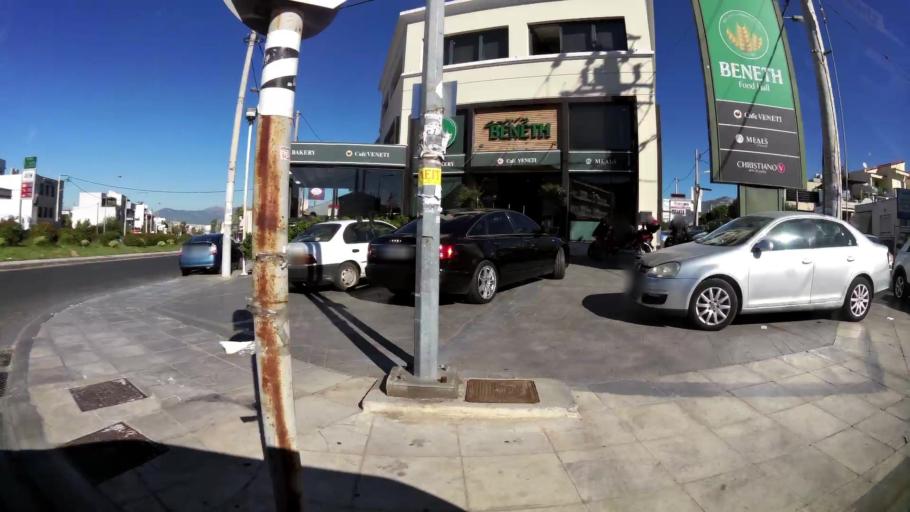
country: GR
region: Attica
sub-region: Nomarchia Athinas
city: Agia Paraskevi
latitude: 38.0141
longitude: 23.8435
